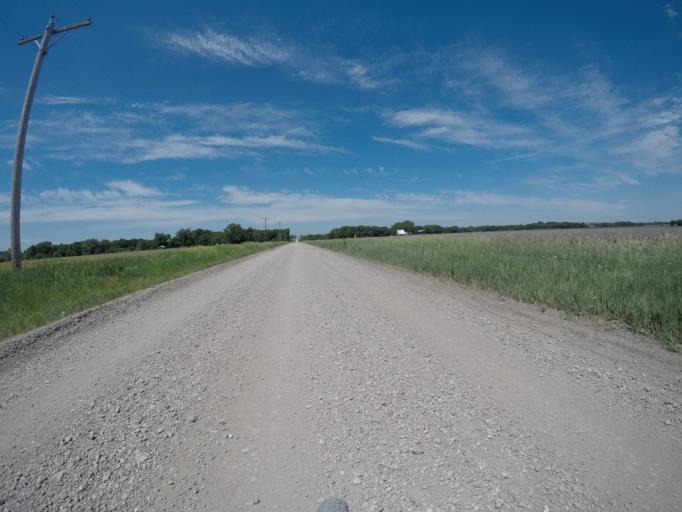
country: US
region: Kansas
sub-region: Wabaunsee County
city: Alma
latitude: 39.0581
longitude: -96.2291
